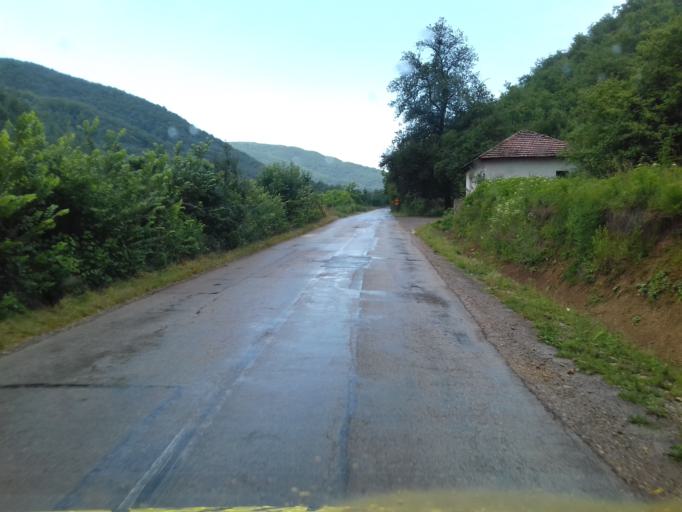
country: BA
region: Federation of Bosnia and Herzegovina
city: Visoko
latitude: 43.9551
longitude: 18.1526
